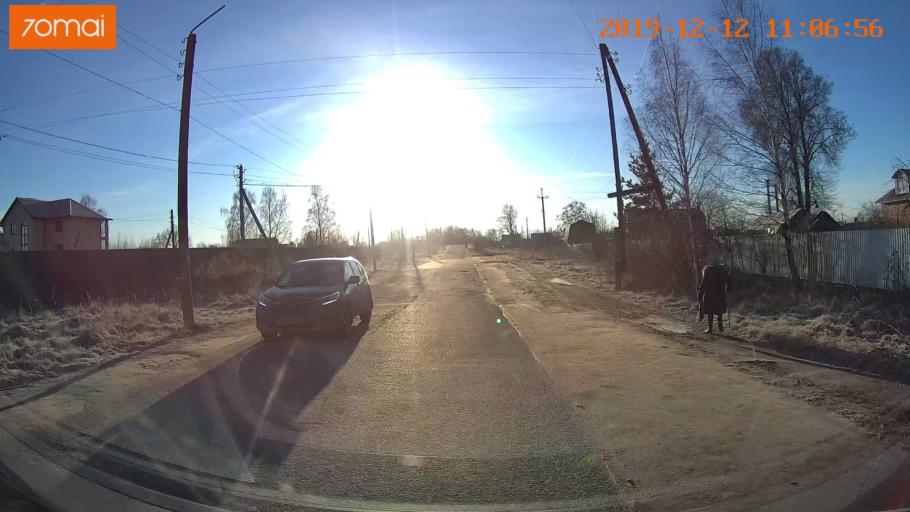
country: RU
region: Ivanovo
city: Kokhma
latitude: 56.9404
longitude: 41.0885
